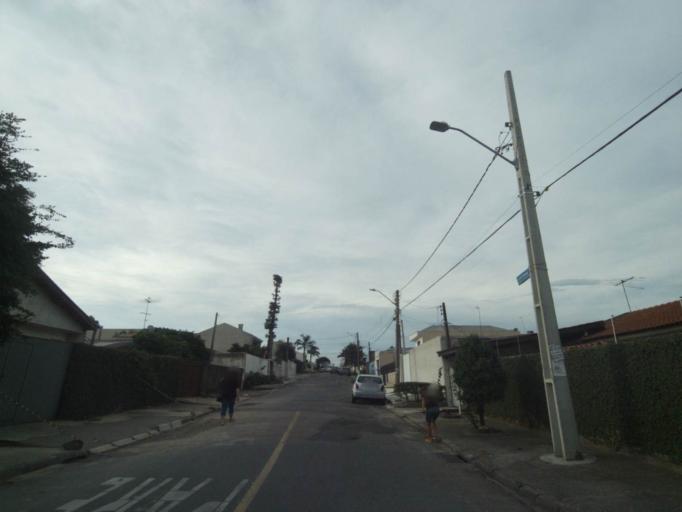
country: BR
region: Parana
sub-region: Pinhais
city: Pinhais
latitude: -25.4648
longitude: -49.2146
